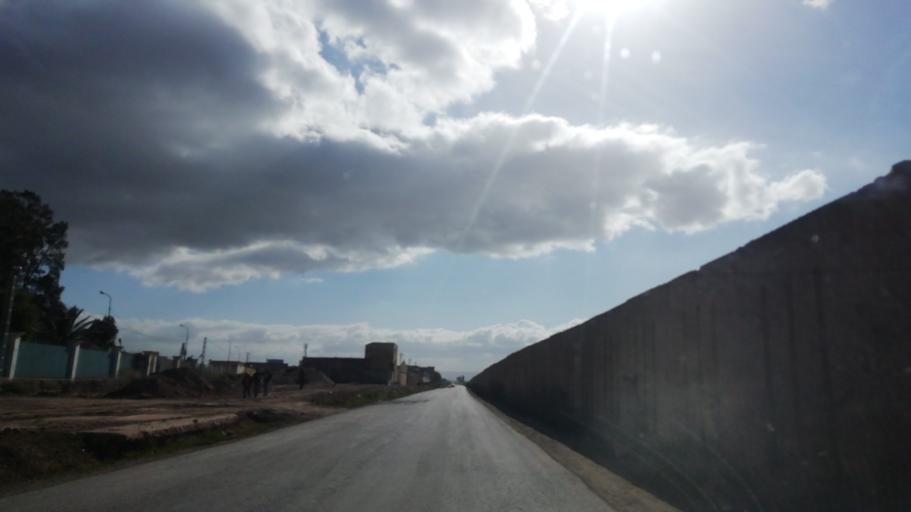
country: DZ
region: Oran
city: Es Senia
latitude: 35.6479
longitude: -0.6057
